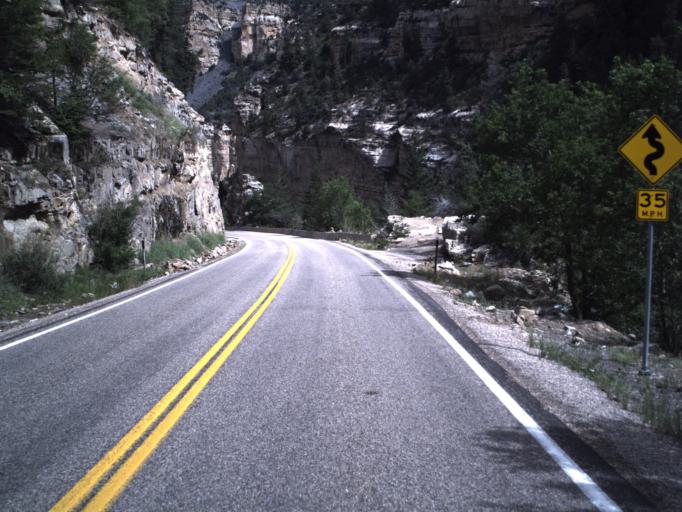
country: US
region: Utah
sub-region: Iron County
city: Cedar City
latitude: 37.6256
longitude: -112.9334
